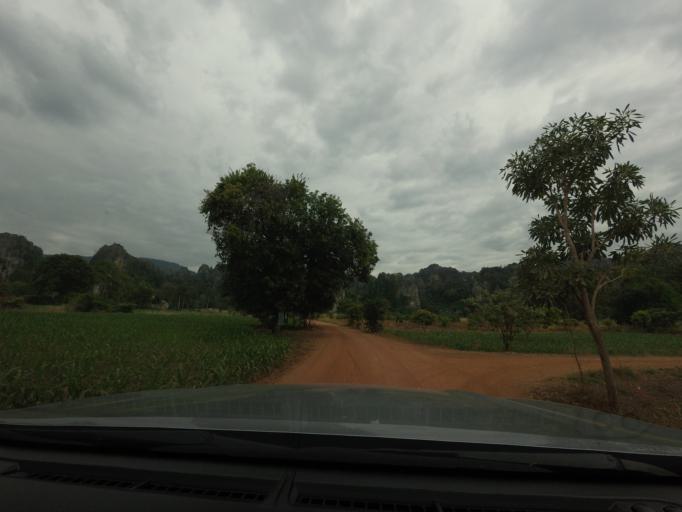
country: TH
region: Phitsanulok
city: Noen Maprang
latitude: 16.5789
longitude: 100.6835
